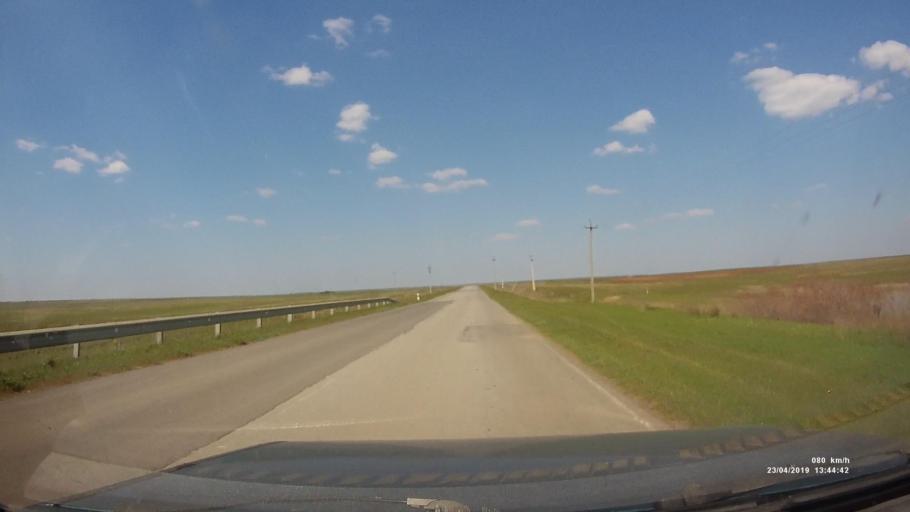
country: RU
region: Kalmykiya
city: Yashalta
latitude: 46.5840
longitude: 42.8178
